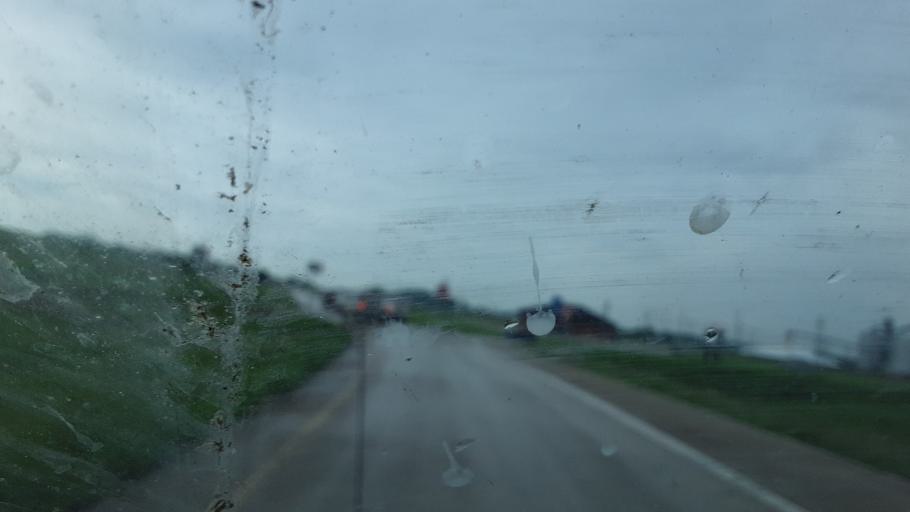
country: US
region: Illinois
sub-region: Hancock County
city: Warsaw
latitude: 40.3946
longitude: -91.5740
